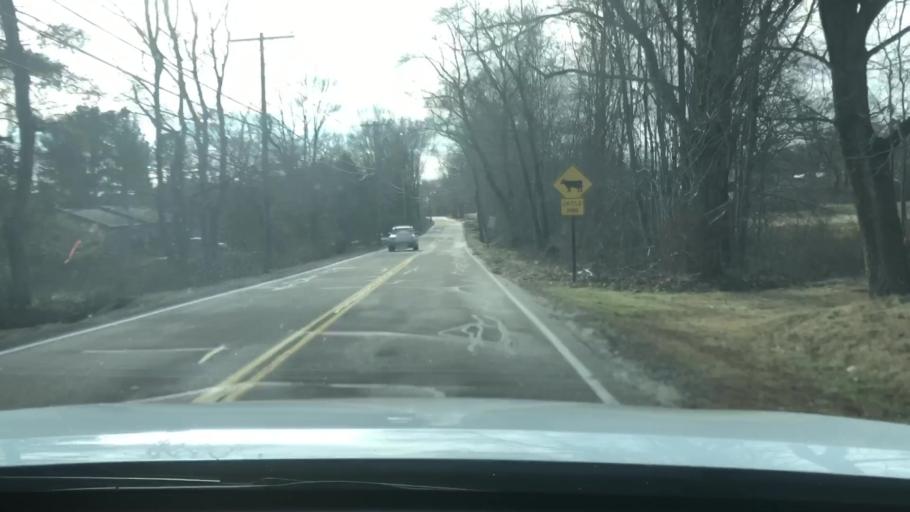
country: US
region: Massachusetts
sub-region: Worcester County
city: Blackstone
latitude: 42.0291
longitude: -71.5247
